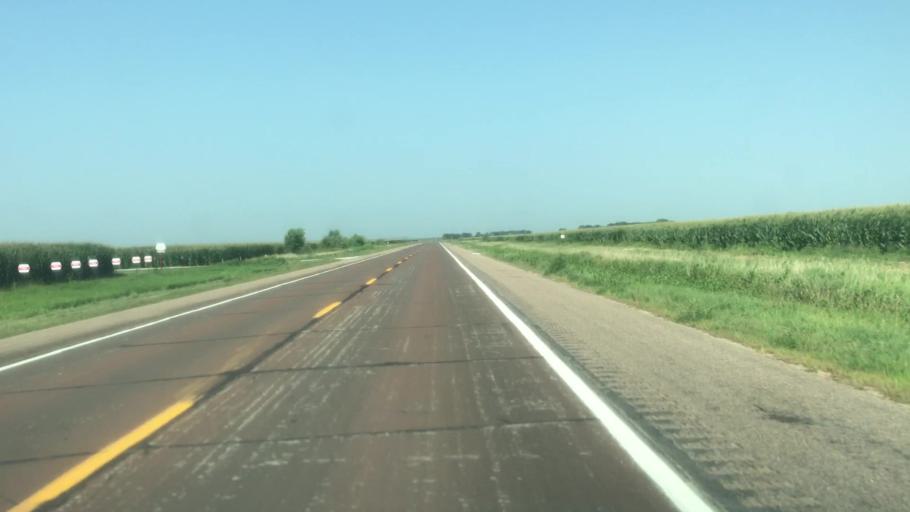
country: US
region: Nebraska
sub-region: Hall County
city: Grand Island
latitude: 40.9677
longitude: -98.4801
